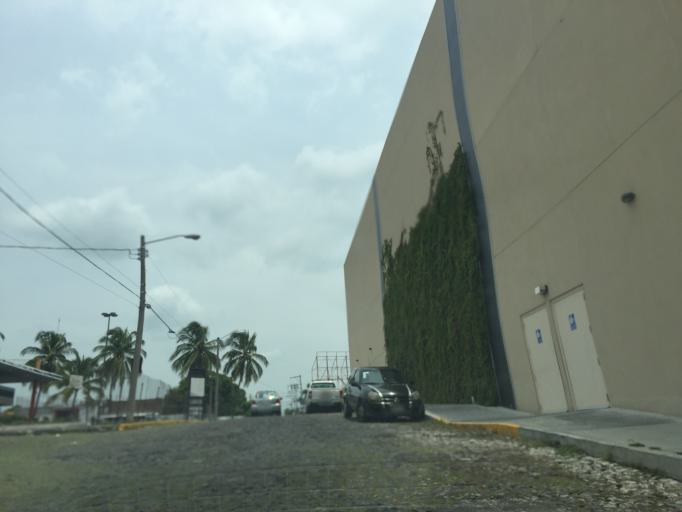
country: MX
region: Colima
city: Colima
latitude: 19.2534
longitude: -103.7203
